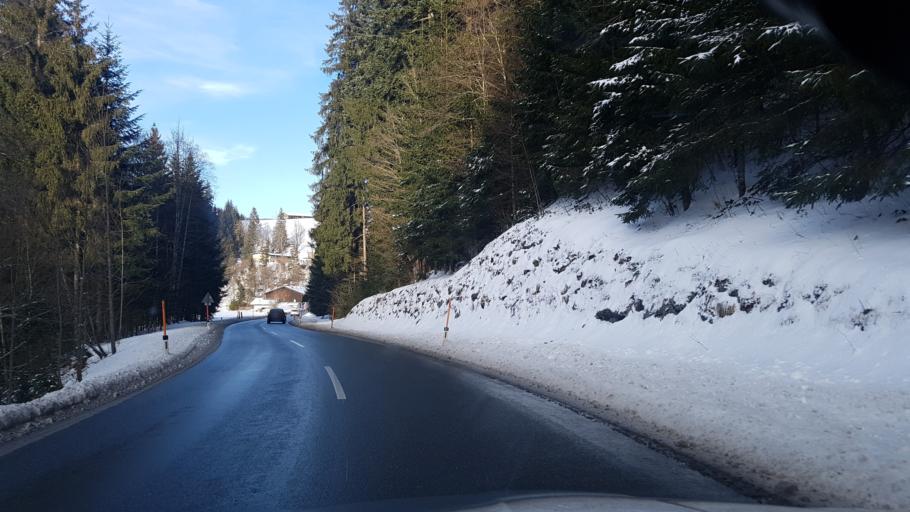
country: AT
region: Tyrol
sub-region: Politischer Bezirk Kitzbuhel
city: Oberndorf in Tirol
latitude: 47.5020
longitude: 12.3581
